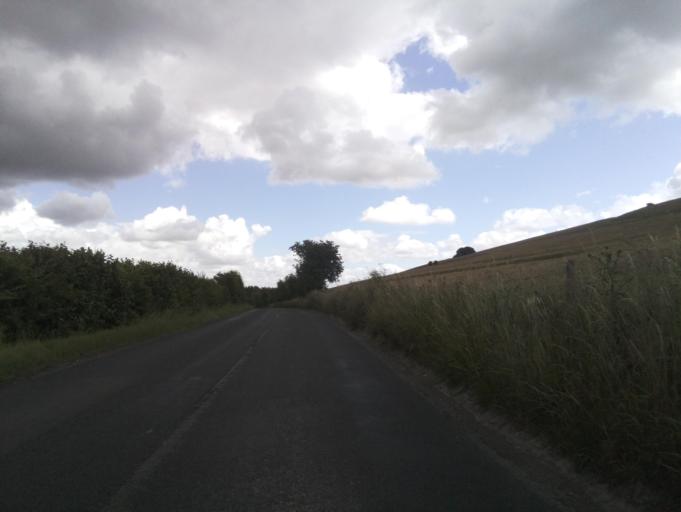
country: GB
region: England
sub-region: Borough of Swindon
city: Wanborough
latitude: 51.5184
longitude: -1.7034
